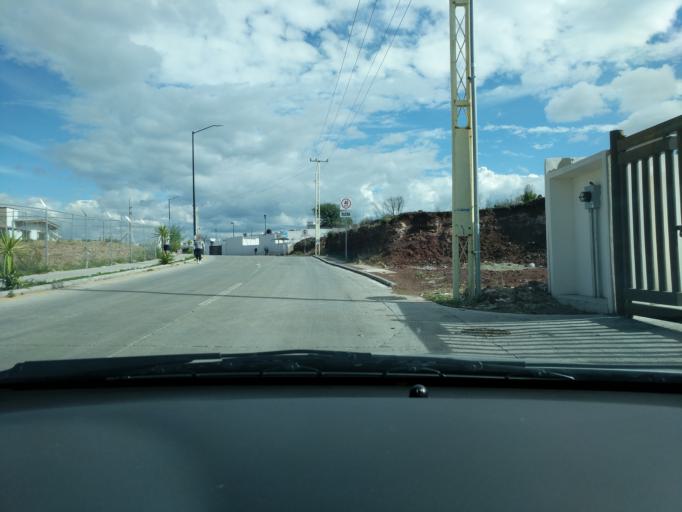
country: MX
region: Queretaro
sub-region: El Marques
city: La Loma
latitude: 20.5856
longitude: -100.2627
